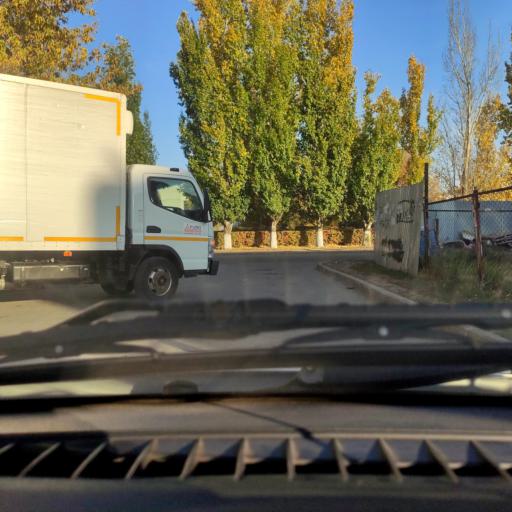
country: RU
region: Samara
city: Tol'yatti
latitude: 53.5383
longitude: 49.3377
